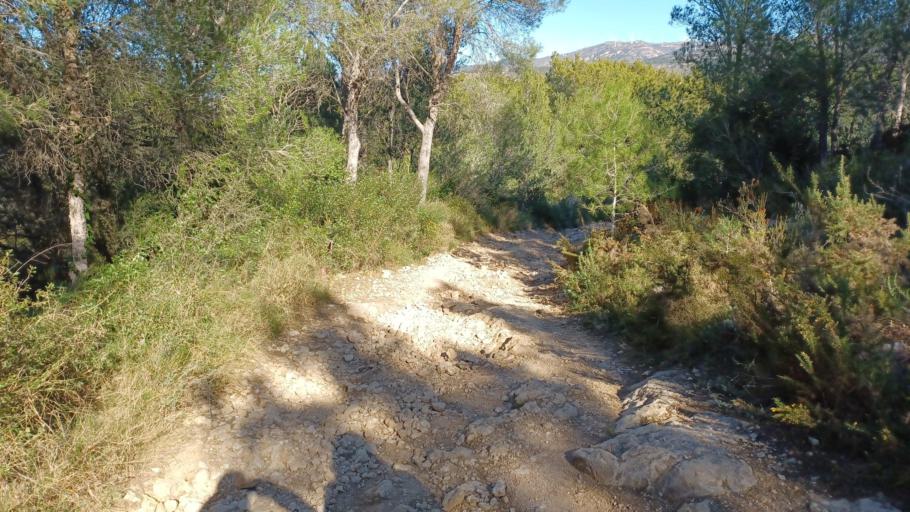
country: ES
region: Catalonia
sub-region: Provincia de Tarragona
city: Tortosa
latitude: 40.8151
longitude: 0.5706
